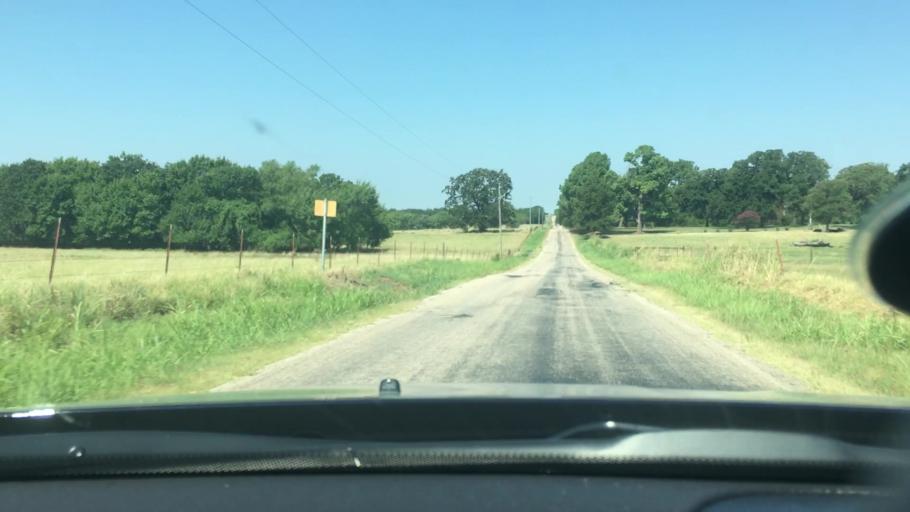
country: US
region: Oklahoma
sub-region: Johnston County
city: Tishomingo
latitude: 34.3176
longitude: -96.6416
